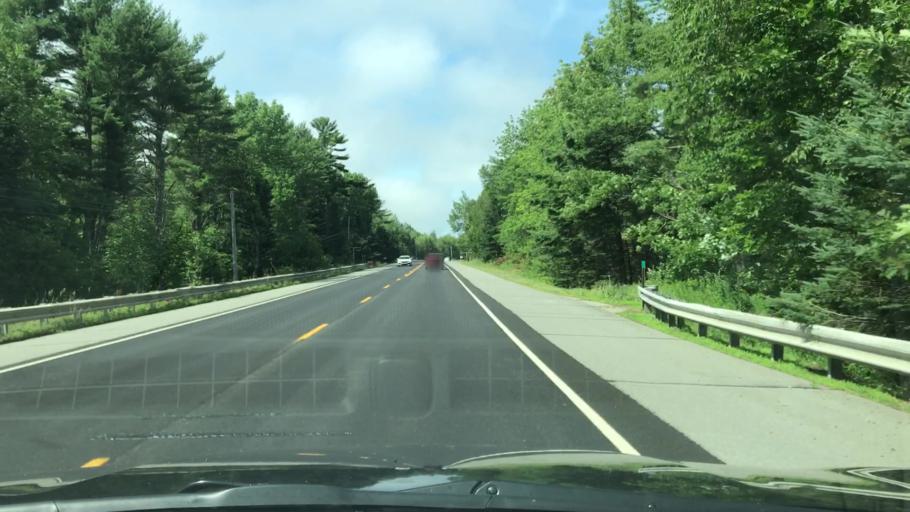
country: US
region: Maine
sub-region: Hancock County
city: Bucksport
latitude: 44.5389
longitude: -68.8094
